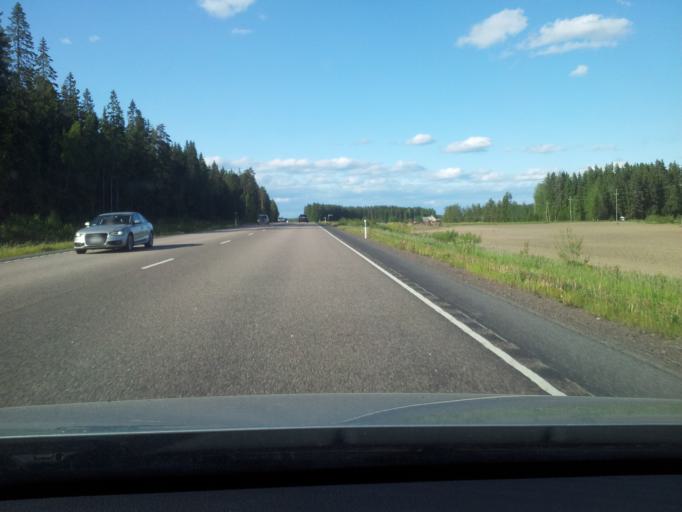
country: FI
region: Kymenlaakso
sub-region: Kouvola
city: Elimaeki
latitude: 60.7811
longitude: 26.4905
